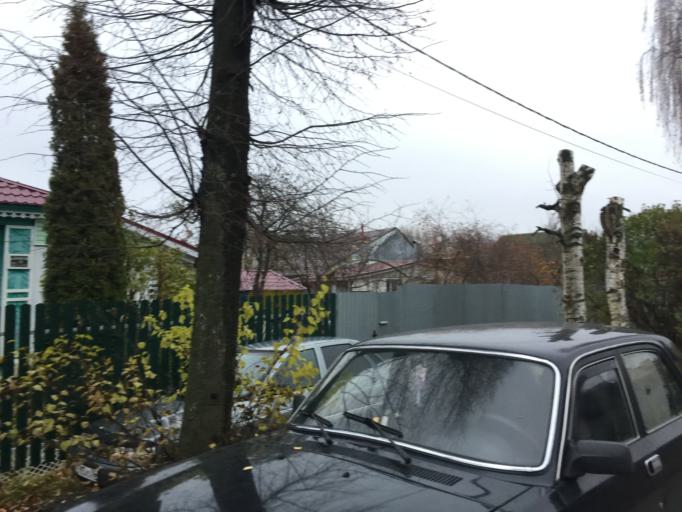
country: RU
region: Jaroslavl
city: Yaroslavl
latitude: 57.7215
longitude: 39.7738
